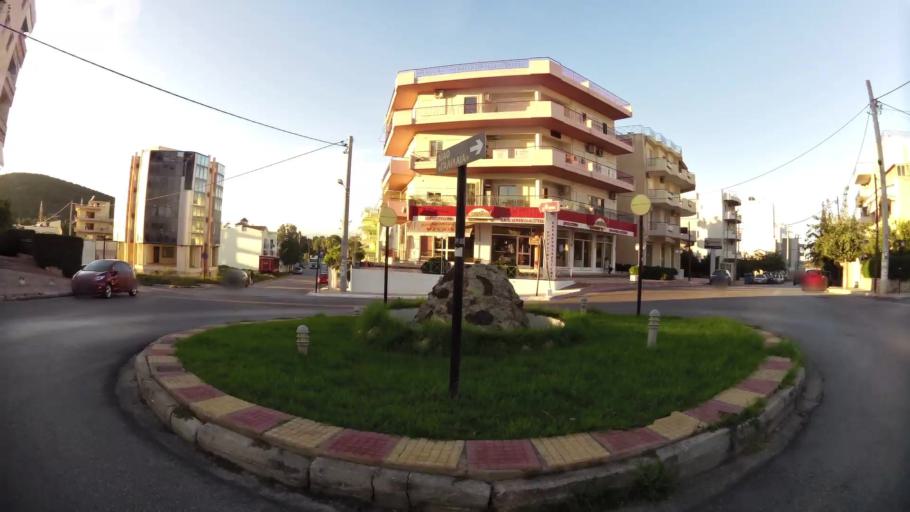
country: GR
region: Attica
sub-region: Nomarchia Anatolikis Attikis
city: Spata
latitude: 37.9665
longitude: 23.9087
